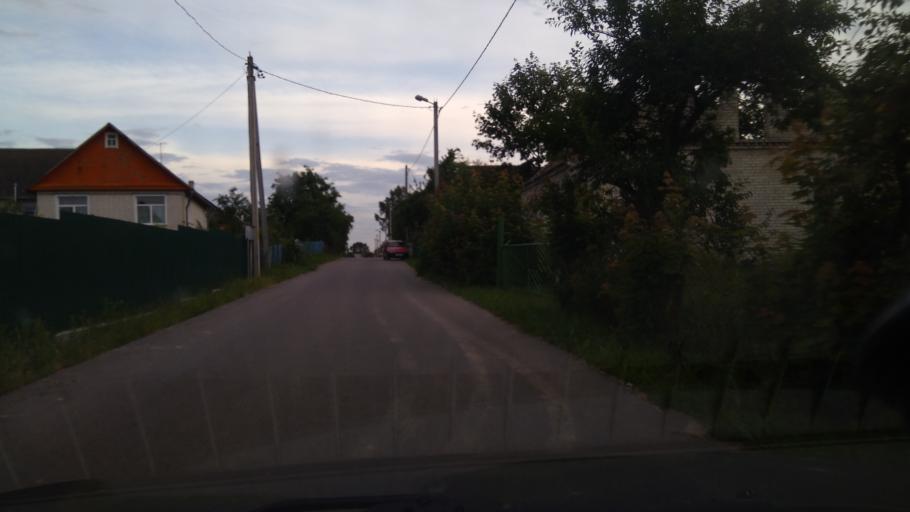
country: BY
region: Grodnenskaya
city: Shchuchin
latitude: 53.5363
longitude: 24.7295
